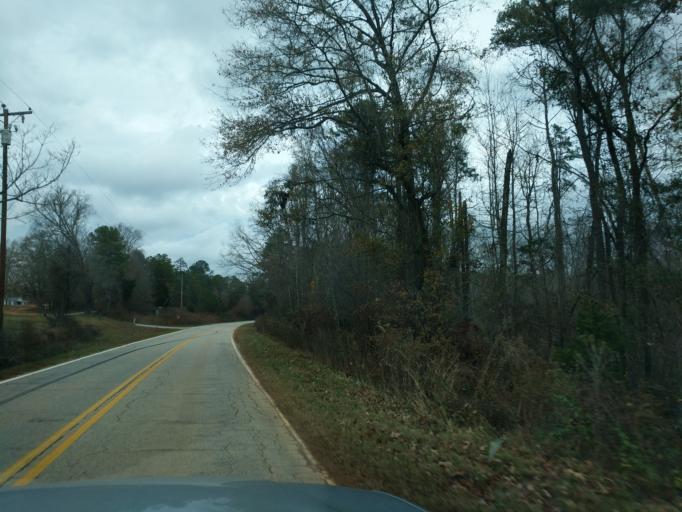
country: US
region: South Carolina
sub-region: Greenwood County
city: Ware Shoals
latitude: 34.3976
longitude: -82.1379
